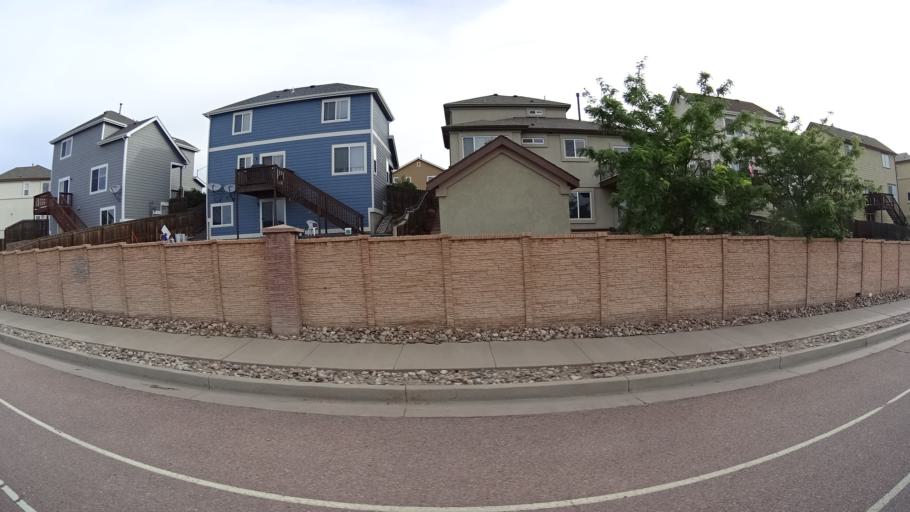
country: US
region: Colorado
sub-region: El Paso County
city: Fountain
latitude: 38.7154
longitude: -104.6937
